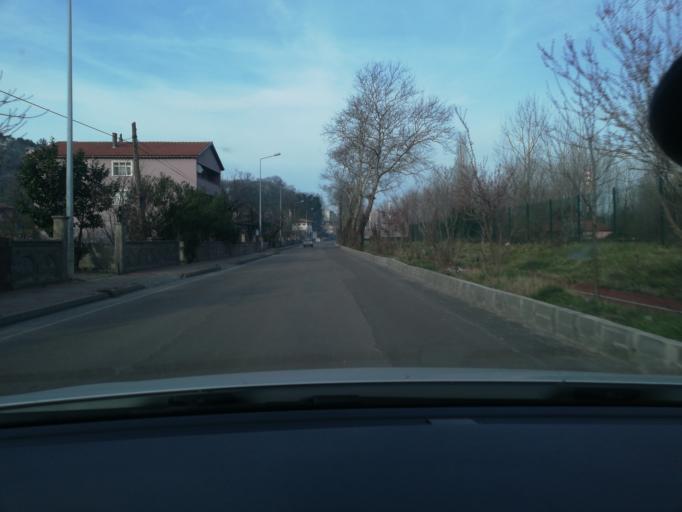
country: TR
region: Zonguldak
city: Kilimli
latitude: 41.5071
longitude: 31.8866
